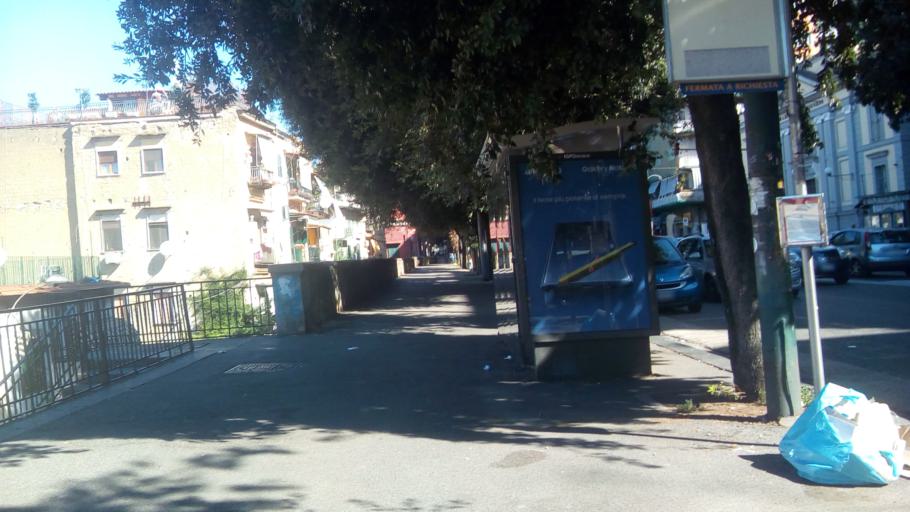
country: IT
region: Campania
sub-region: Provincia di Napoli
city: Napoli
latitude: 40.8592
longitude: 14.2484
